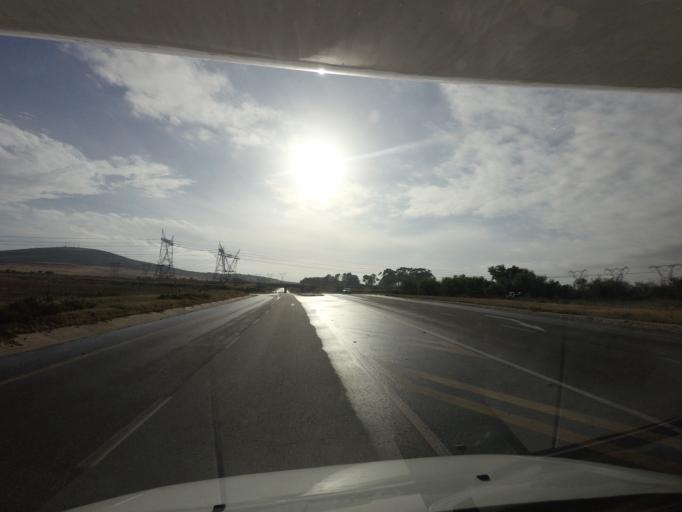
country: ZA
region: Western Cape
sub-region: City of Cape Town
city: Sunset Beach
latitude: -33.7255
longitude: 18.5417
